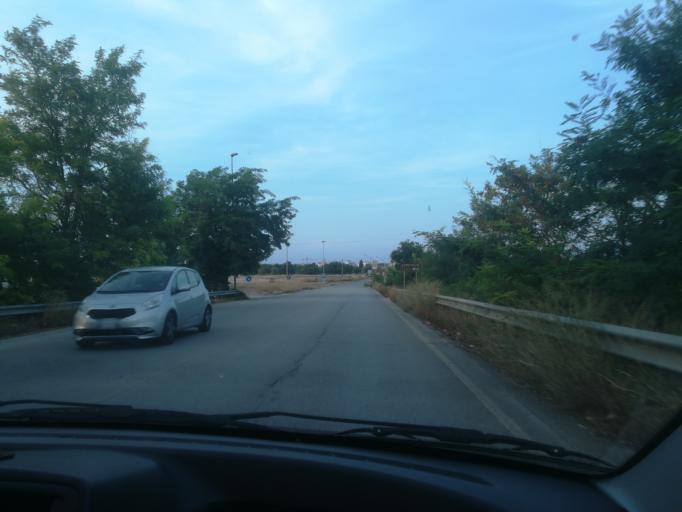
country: IT
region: Apulia
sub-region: Provincia di Bari
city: Monopoli
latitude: 40.9363
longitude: 17.2928
